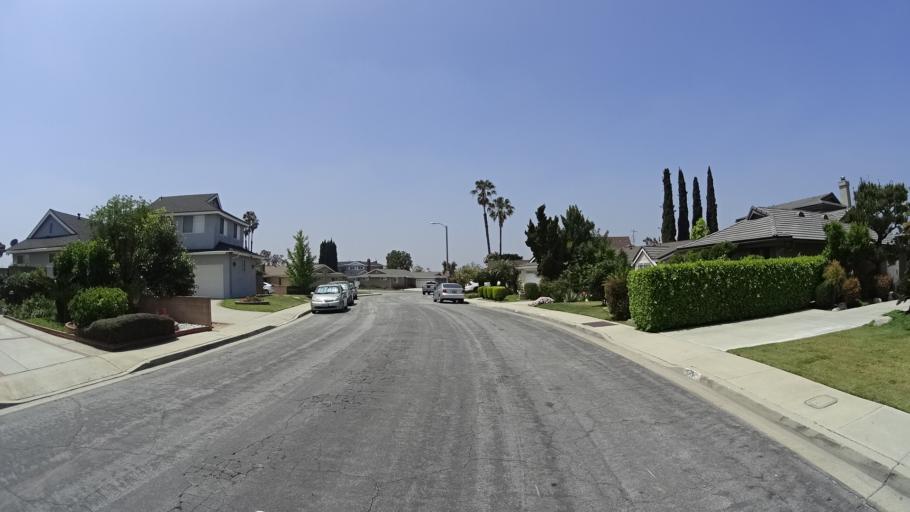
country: US
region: California
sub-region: Los Angeles County
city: Belvedere
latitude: 34.0558
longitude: -118.1537
